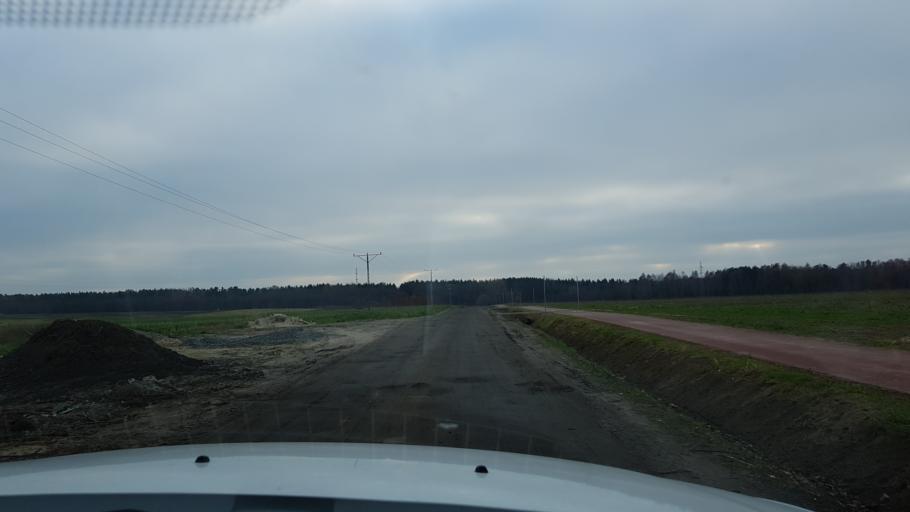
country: PL
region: West Pomeranian Voivodeship
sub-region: Powiat kolobrzeski
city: Grzybowo
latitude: 54.1403
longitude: 15.5149
